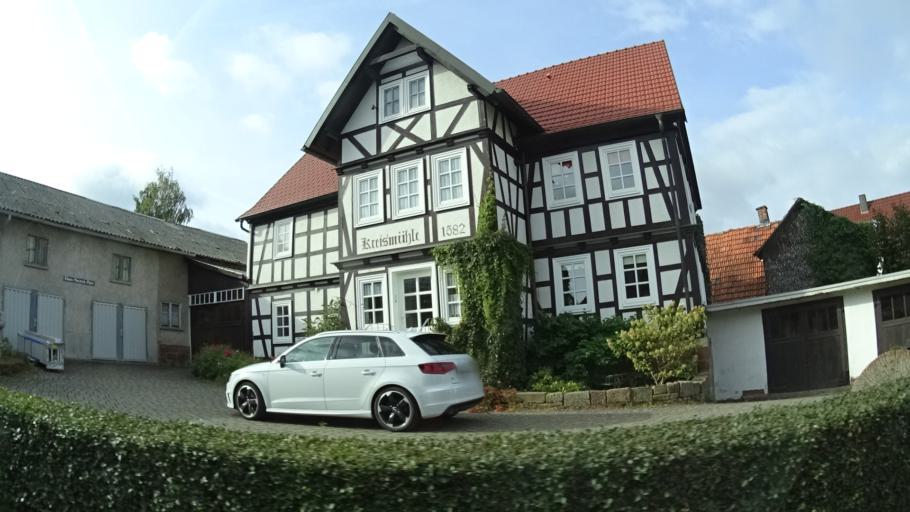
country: DE
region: Thuringia
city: Oberweid
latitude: 50.5916
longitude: 10.0631
